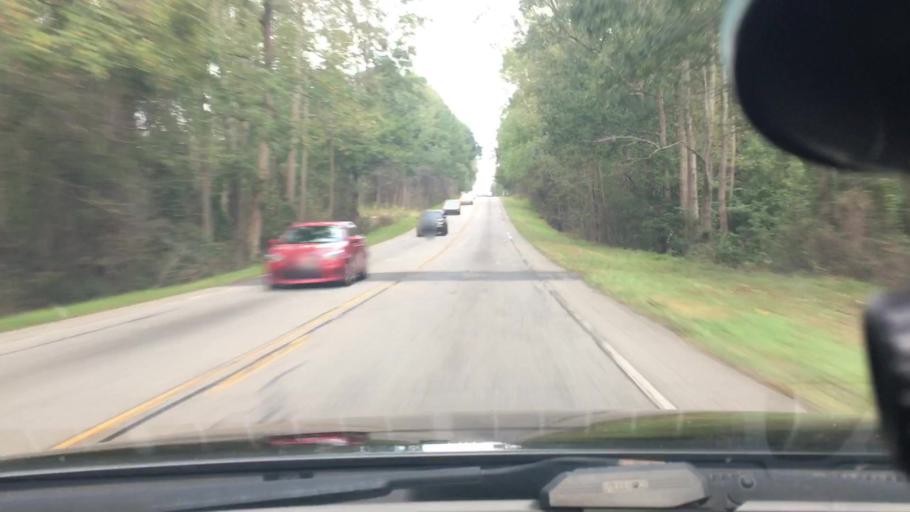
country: US
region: North Carolina
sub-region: Moore County
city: Carthage
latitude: 35.3483
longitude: -79.3700
